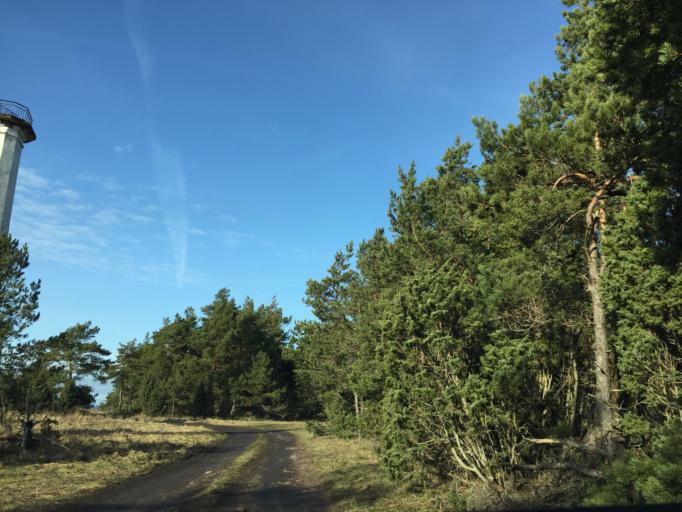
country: EE
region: Saare
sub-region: Kuressaare linn
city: Kuressaare
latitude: 58.3756
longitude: 21.9998
